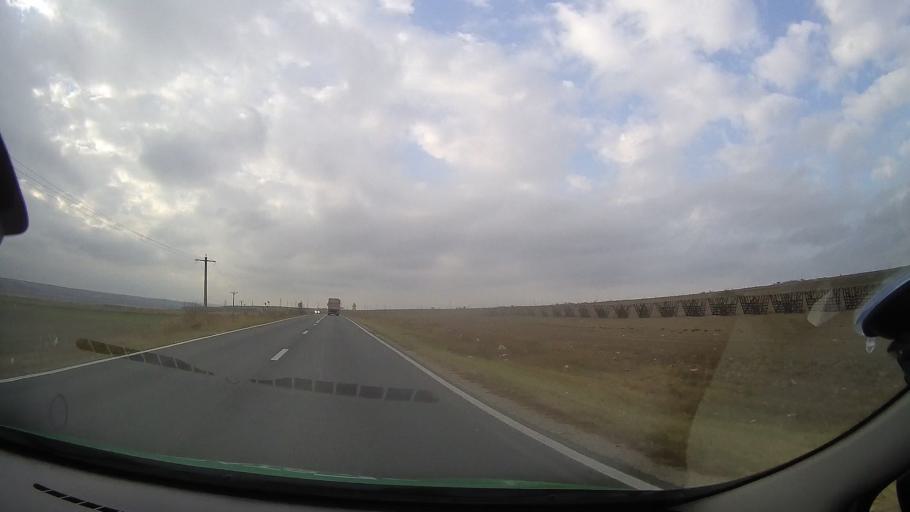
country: RO
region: Constanta
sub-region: Comuna Mircea Voda
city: Satu Nou
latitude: 44.2697
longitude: 28.2153
